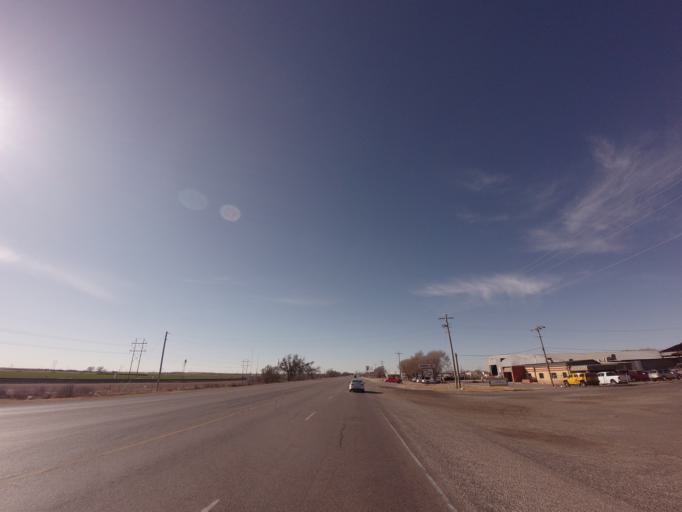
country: US
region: New Mexico
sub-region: Curry County
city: Clovis
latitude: 34.3943
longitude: -103.1452
